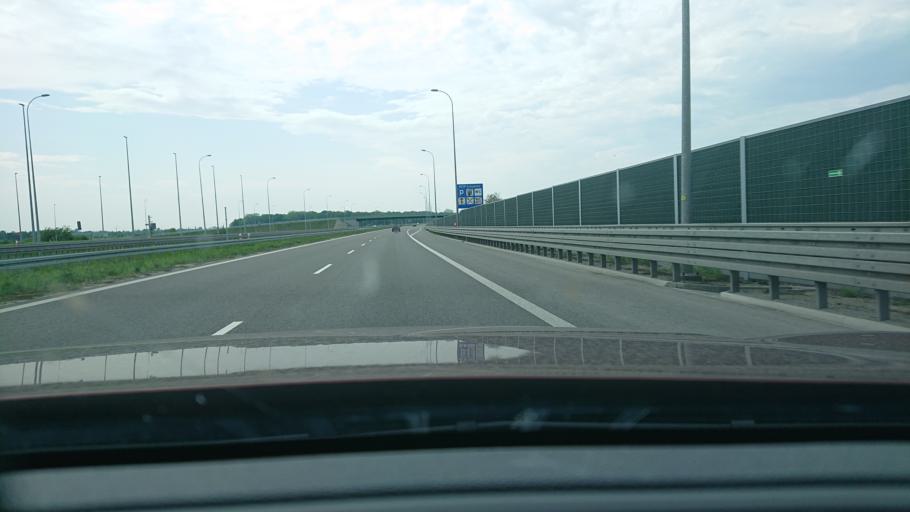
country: PL
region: Subcarpathian Voivodeship
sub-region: Powiat lancucki
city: Czarna
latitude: 50.0904
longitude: 22.1651
